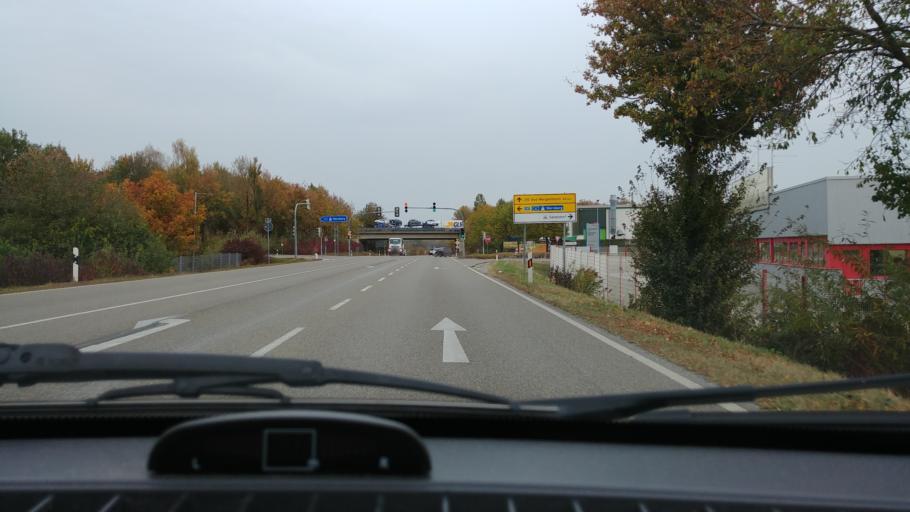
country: DE
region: Baden-Wuerttemberg
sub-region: Regierungsbezirk Stuttgart
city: Satteldorf
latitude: 49.1814
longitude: 10.0712
